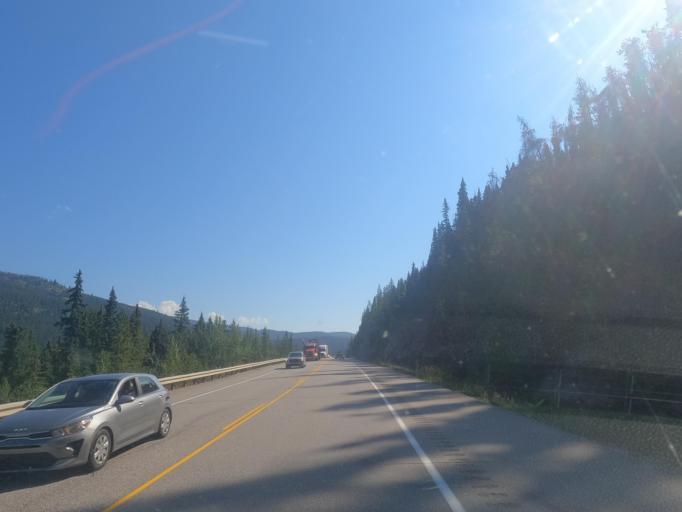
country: CA
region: Alberta
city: Jasper Park Lodge
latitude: 52.8725
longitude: -118.2926
